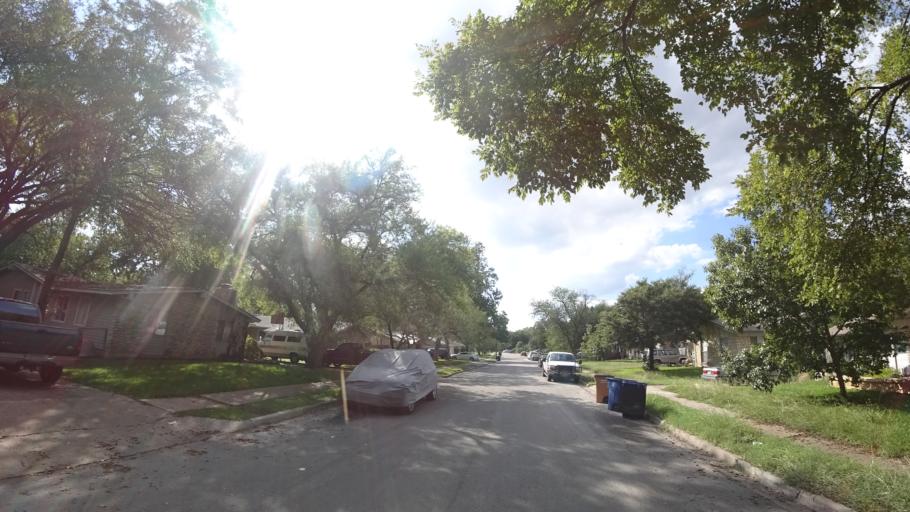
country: US
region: Texas
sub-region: Travis County
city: Wells Branch
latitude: 30.3573
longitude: -97.7021
